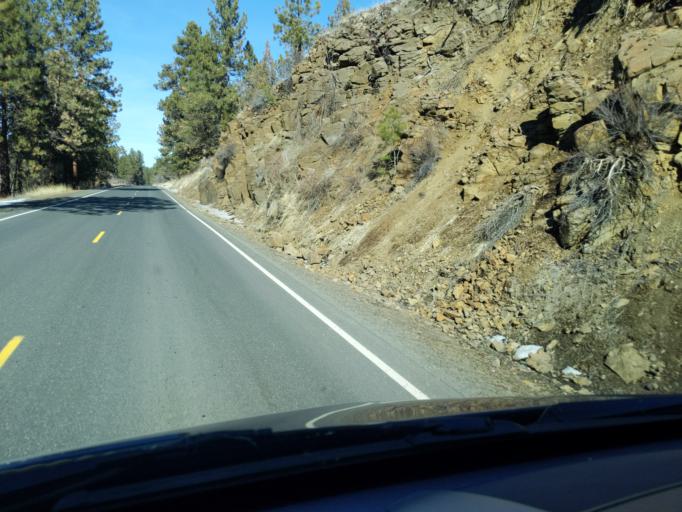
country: US
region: Oregon
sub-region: Grant County
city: John Day
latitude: 44.8635
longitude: -119.0257
